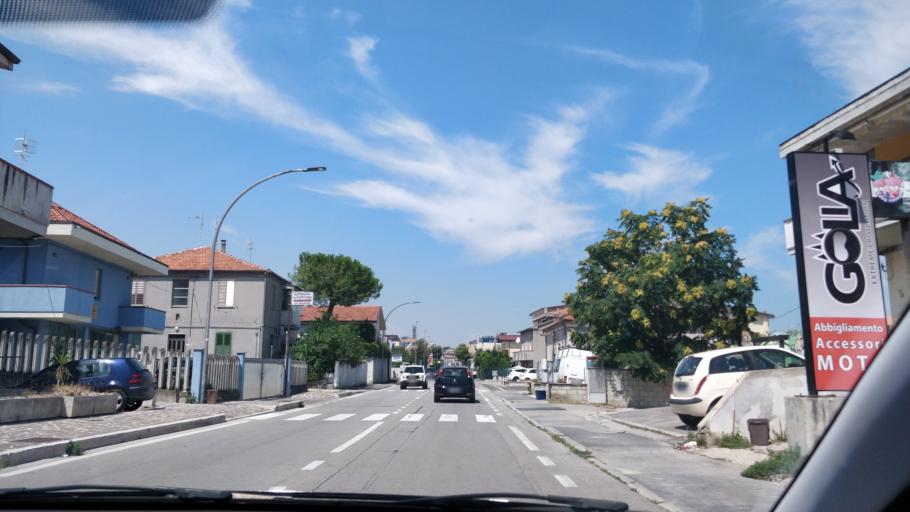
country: IT
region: Abruzzo
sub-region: Provincia di Chieti
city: Francavilla al Mare
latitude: 42.4118
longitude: 14.3030
